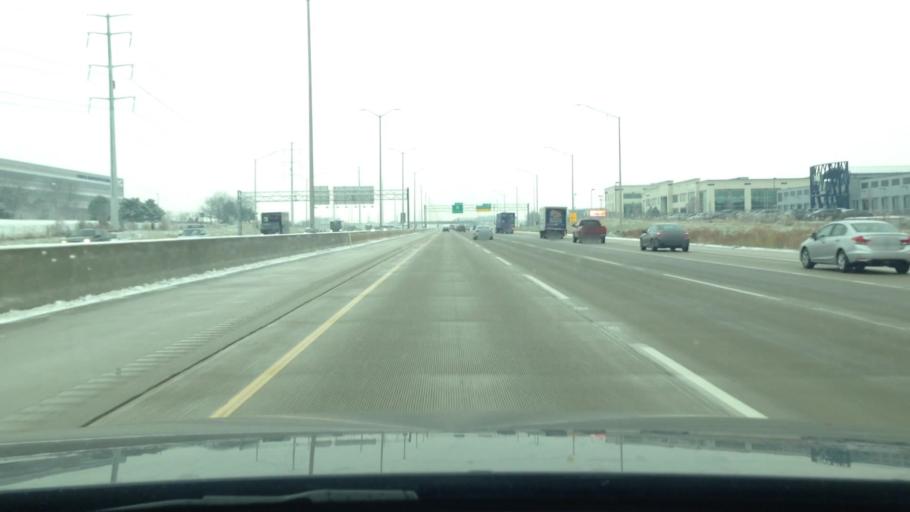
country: US
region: Illinois
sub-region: Kane County
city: Sleepy Hollow
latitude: 42.0768
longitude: -88.3263
